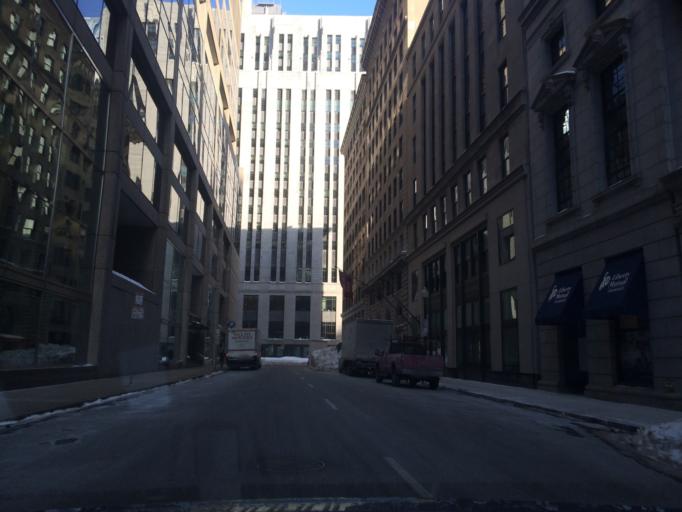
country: US
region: Massachusetts
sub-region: Suffolk County
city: Boston
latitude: 42.3555
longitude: -71.0566
